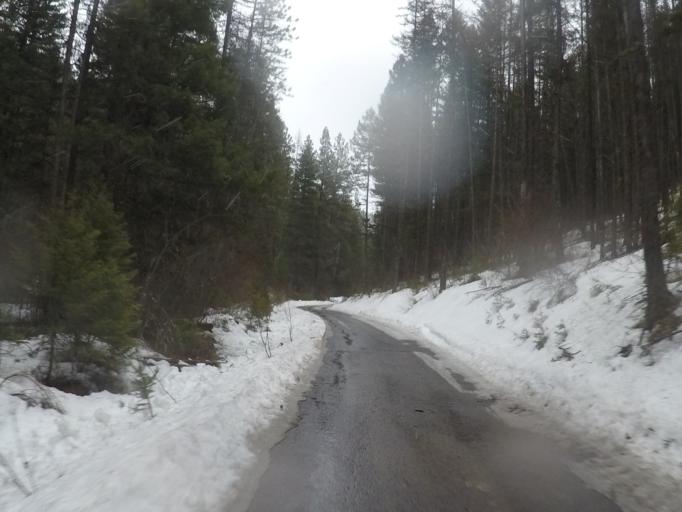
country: US
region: Montana
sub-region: Missoula County
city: Missoula
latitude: 46.9299
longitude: -113.9695
